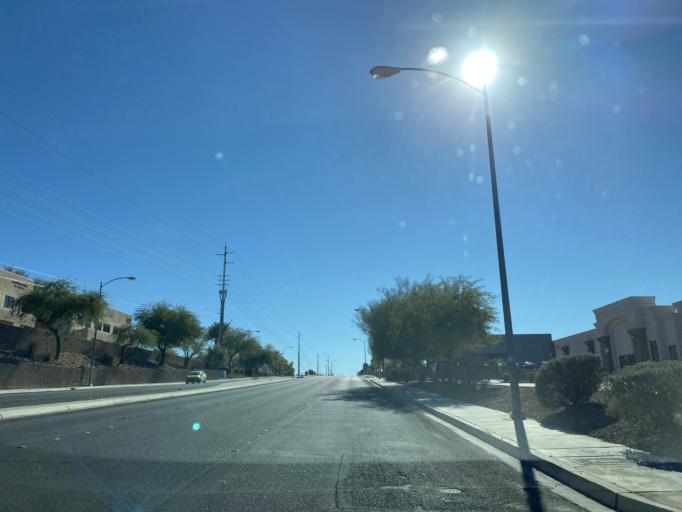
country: US
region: Nevada
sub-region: Clark County
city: Whitney
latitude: 36.0764
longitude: -115.0825
